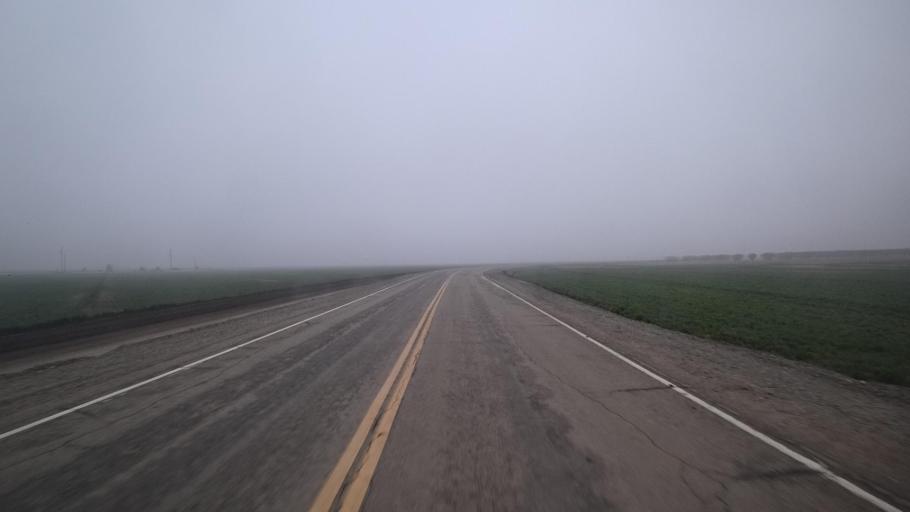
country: US
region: California
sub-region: Kern County
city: Buttonwillow
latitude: 35.4295
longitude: -119.5424
